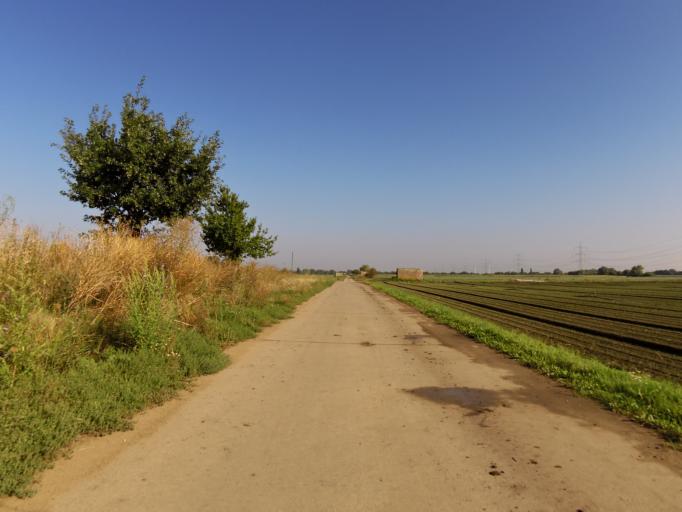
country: DE
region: Rheinland-Pfalz
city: Maxdorf
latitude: 49.4874
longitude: 8.3036
